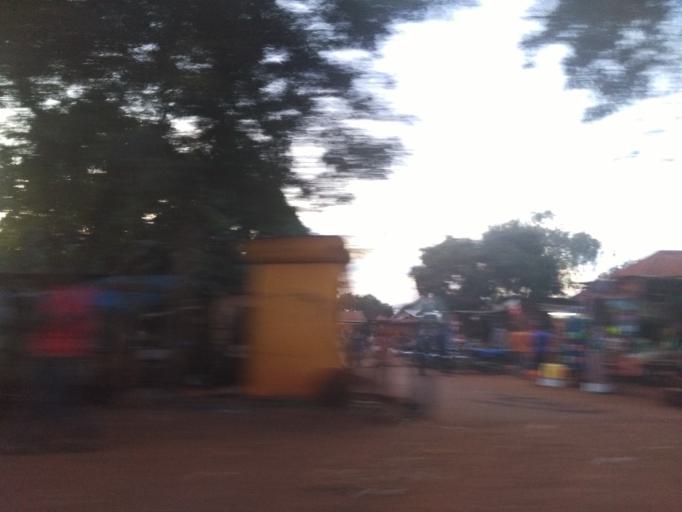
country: UG
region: Eastern Region
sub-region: Jinja District
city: Jinja
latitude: 0.4302
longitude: 33.2065
